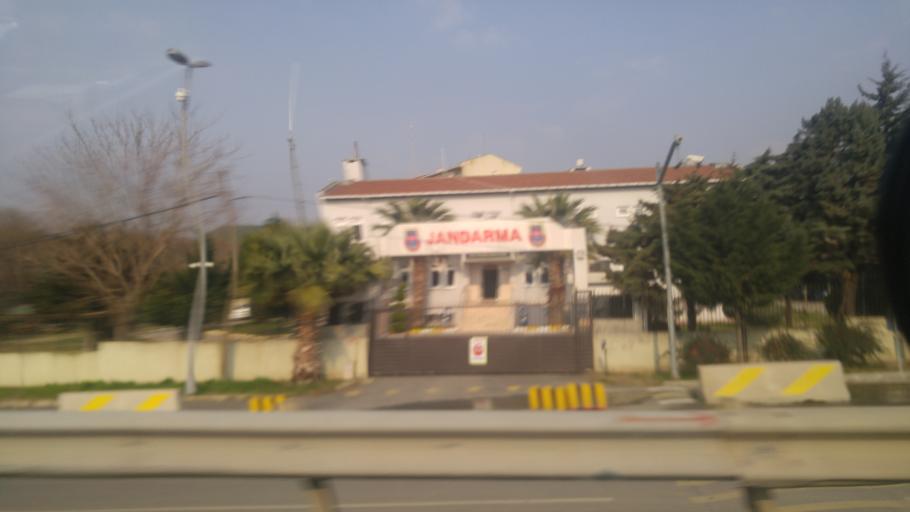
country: TR
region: Istanbul
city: Kumburgaz
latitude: 41.0103
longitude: 28.5011
